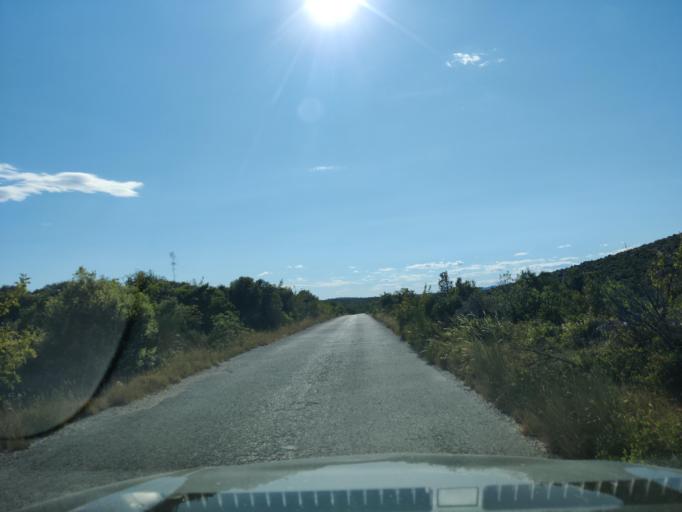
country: HR
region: Sibensko-Kniniska
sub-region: Grad Sibenik
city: Sibenik
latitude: 43.7391
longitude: 15.8688
